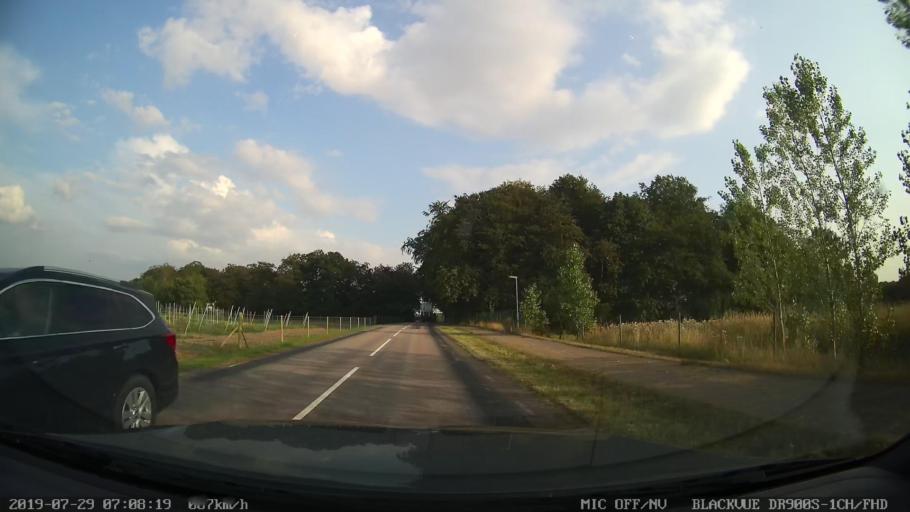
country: SE
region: Skane
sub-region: Helsingborg
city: Odakra
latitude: 56.1001
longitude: 12.6982
